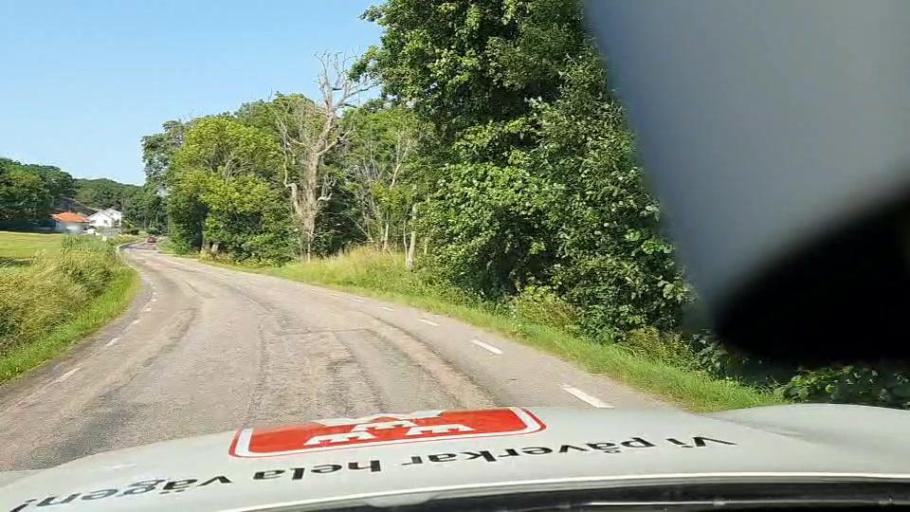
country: SE
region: Vaestra Goetaland
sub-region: Lysekils Kommun
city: Lysekil
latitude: 58.1371
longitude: 11.4589
